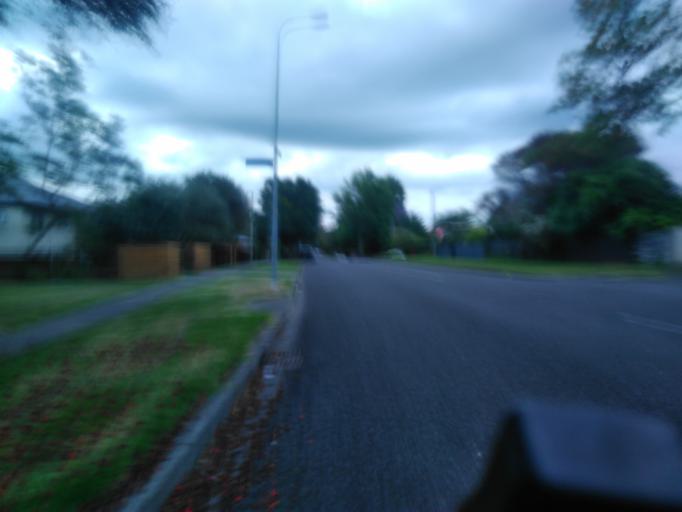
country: NZ
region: Gisborne
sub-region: Gisborne District
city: Gisborne
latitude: -38.6589
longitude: 178.0270
